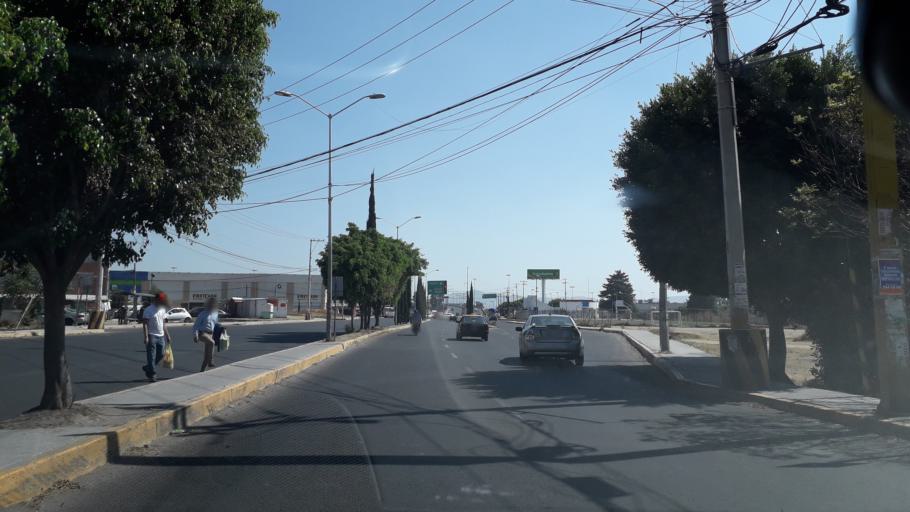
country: MX
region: Puebla
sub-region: Puebla
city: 18 de Marzo
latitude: 18.9837
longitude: -98.2174
